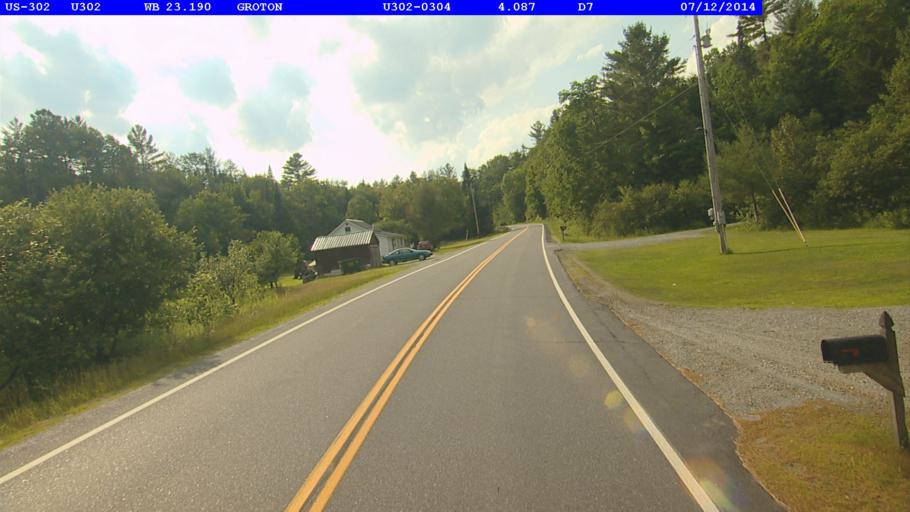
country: US
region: New Hampshire
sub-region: Grafton County
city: Woodsville
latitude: 44.2171
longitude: -72.2390
